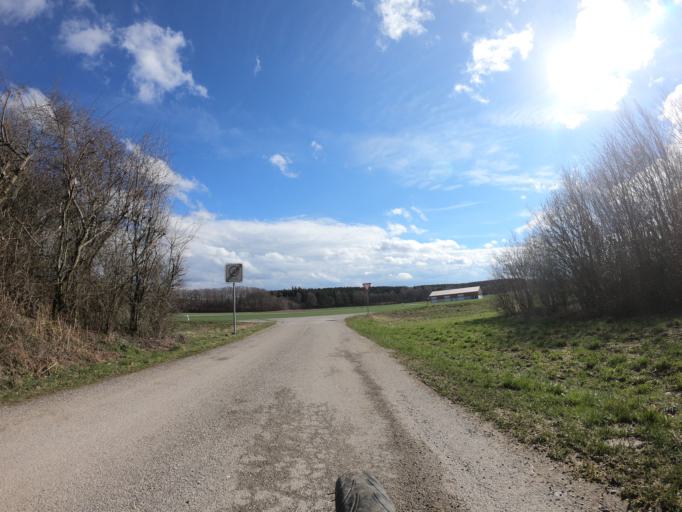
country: DE
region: Bavaria
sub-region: Upper Bavaria
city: Landsberied
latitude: 48.1744
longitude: 11.1819
